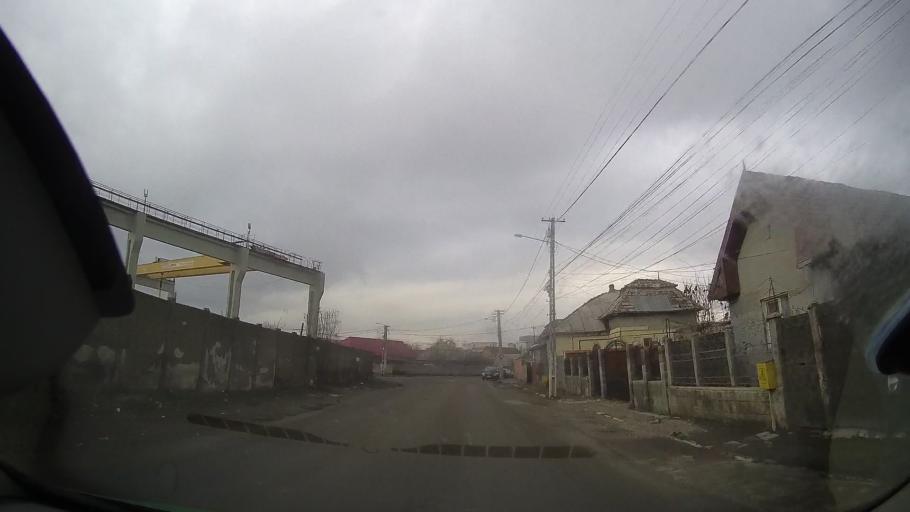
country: RO
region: Cluj
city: Turda
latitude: 46.5562
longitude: 23.7887
